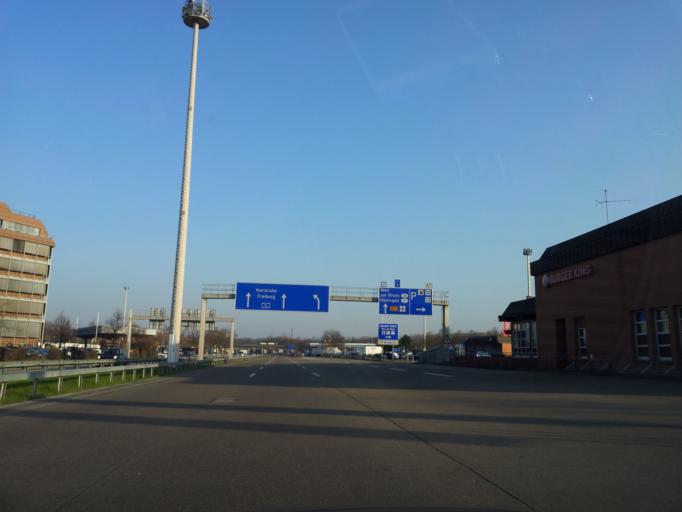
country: DE
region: Baden-Wuerttemberg
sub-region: Freiburg Region
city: Weil am Rhein
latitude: 47.5972
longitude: 7.6037
